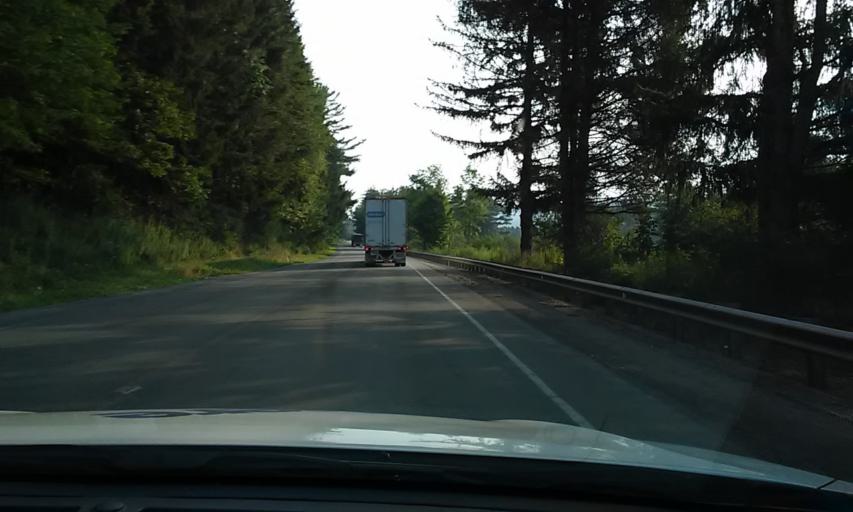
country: US
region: Pennsylvania
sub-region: McKean County
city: Smethport
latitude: 41.7746
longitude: -78.5094
